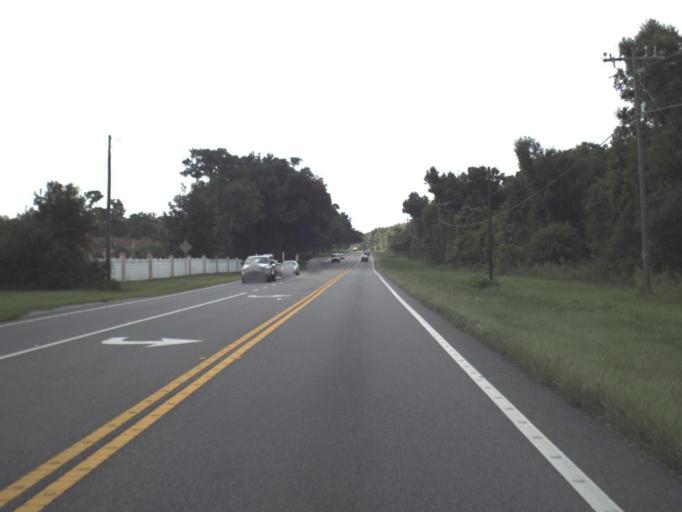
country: US
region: Florida
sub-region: Citrus County
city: Inverness Highlands North
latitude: 28.8771
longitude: -82.3632
